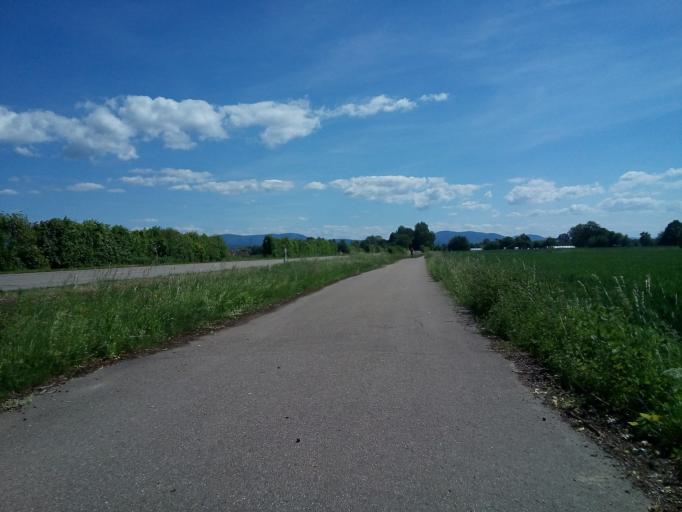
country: DE
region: Baden-Wuerttemberg
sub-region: Freiburg Region
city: Renchen
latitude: 48.6086
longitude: 8.0048
